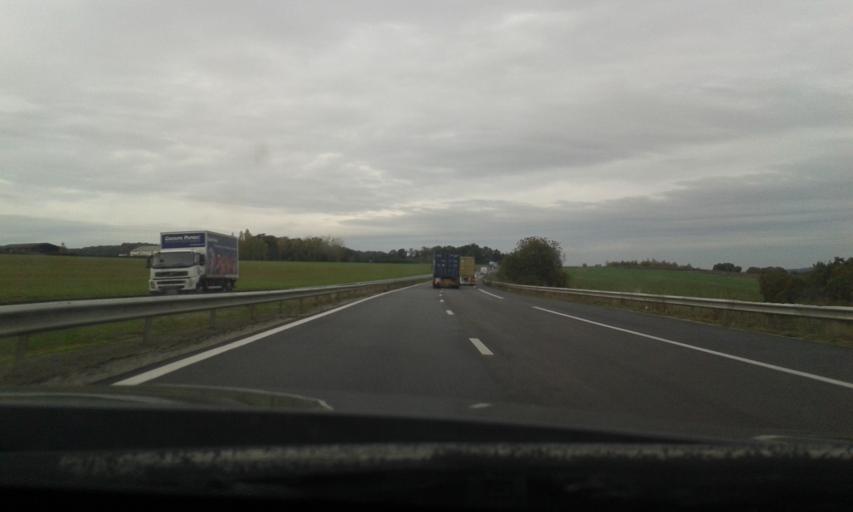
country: FR
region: Haute-Normandie
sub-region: Departement de l'Eure
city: Heudreville-sur-Eure
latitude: 49.1244
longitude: 1.1854
